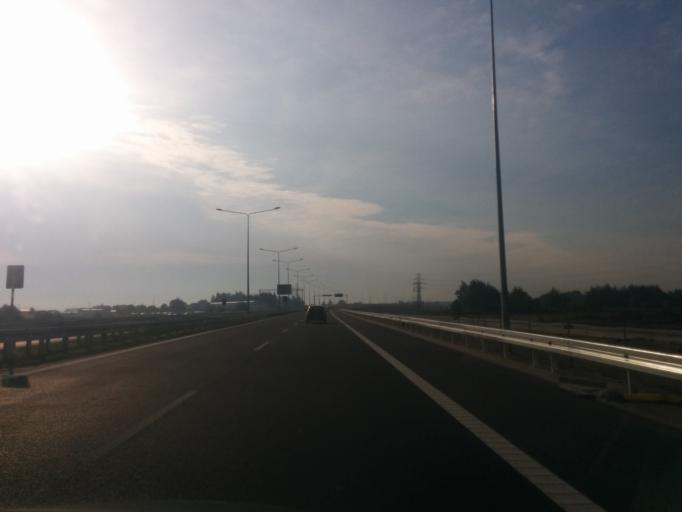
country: PL
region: Masovian Voivodeship
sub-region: Powiat pruszkowski
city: Nowe Grocholice
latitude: 52.1194
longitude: 20.8838
